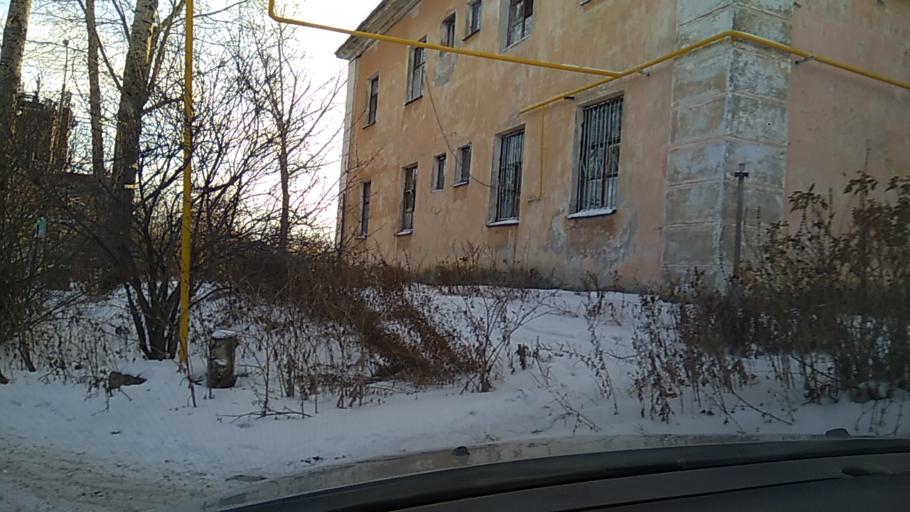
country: RU
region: Sverdlovsk
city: Shirokaya Rechka
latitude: 56.8479
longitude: 60.4993
